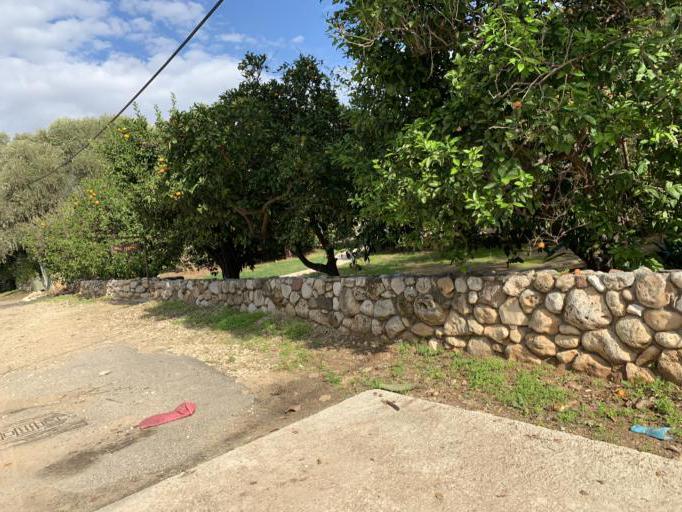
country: IL
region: Central District
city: Ra'anana
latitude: 32.1694
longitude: 34.8754
